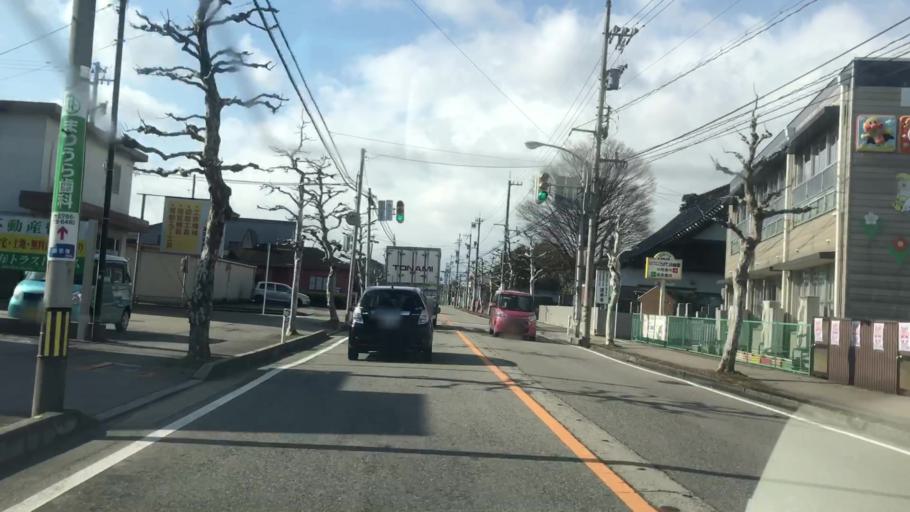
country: JP
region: Toyama
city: Takaoka
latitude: 36.7363
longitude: 137.0379
